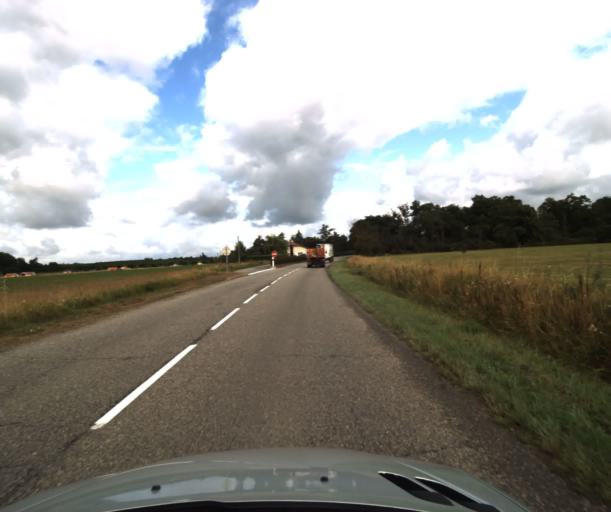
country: FR
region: Midi-Pyrenees
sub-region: Departement du Tarn-et-Garonne
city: Castelsarrasin
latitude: 44.0263
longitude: 1.0591
